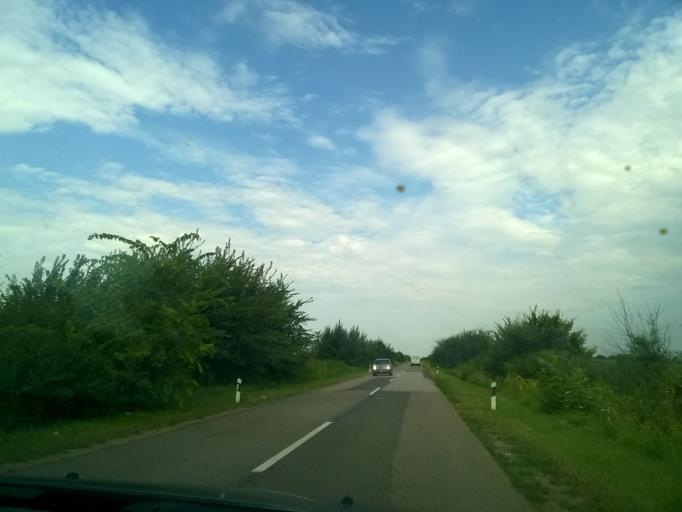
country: RS
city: Stajicevo
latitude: 45.2949
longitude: 20.4995
